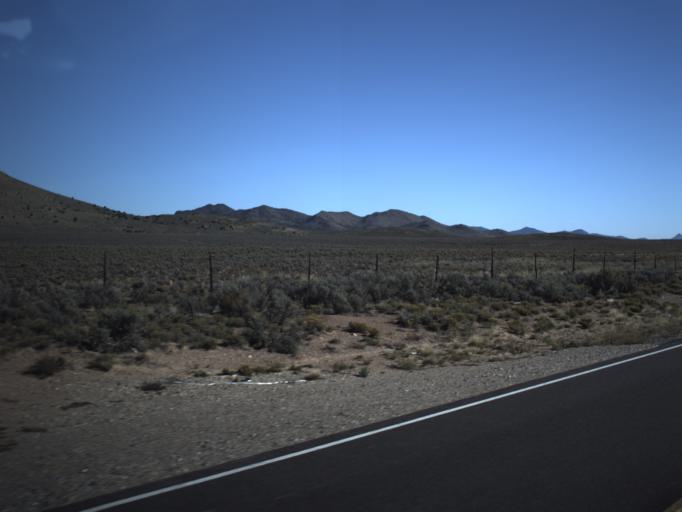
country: US
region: Utah
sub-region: Washington County
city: Enterprise
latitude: 37.7936
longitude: -113.9438
